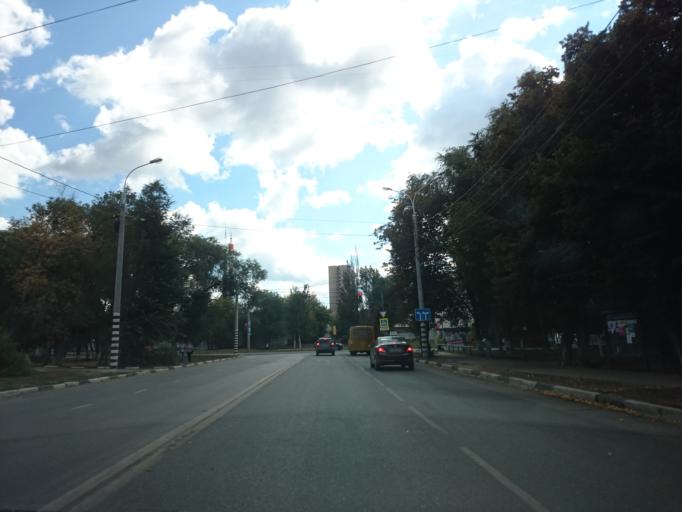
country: RU
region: Samara
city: Samara
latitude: 53.2138
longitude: 50.1412
